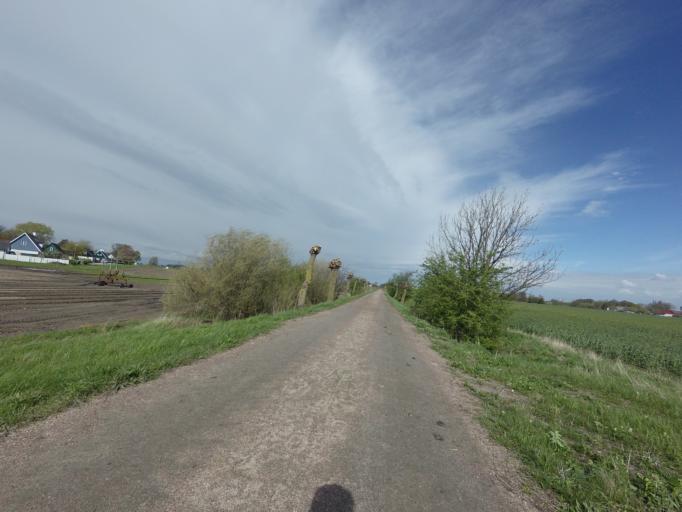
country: SE
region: Skane
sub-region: Malmo
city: Bunkeflostrand
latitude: 55.5391
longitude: 12.9731
